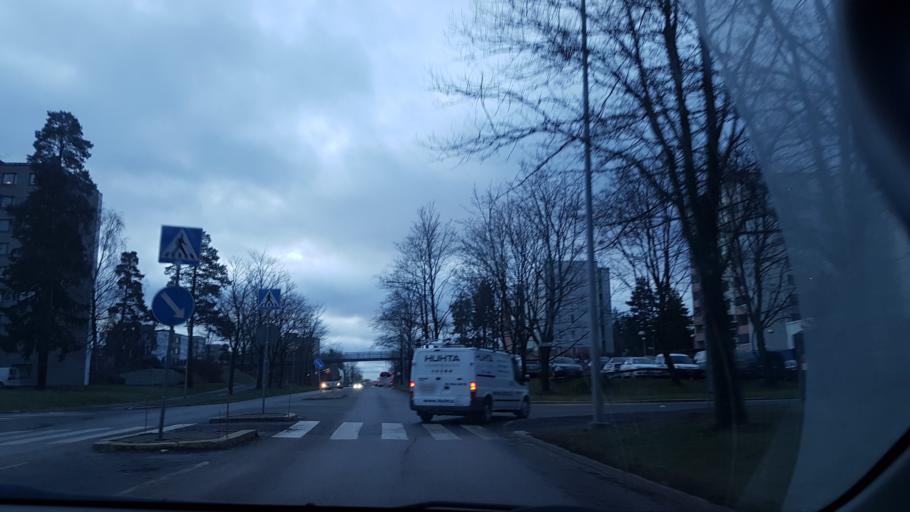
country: FI
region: Uusimaa
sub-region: Helsinki
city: Vantaa
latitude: 60.2756
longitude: 25.1042
